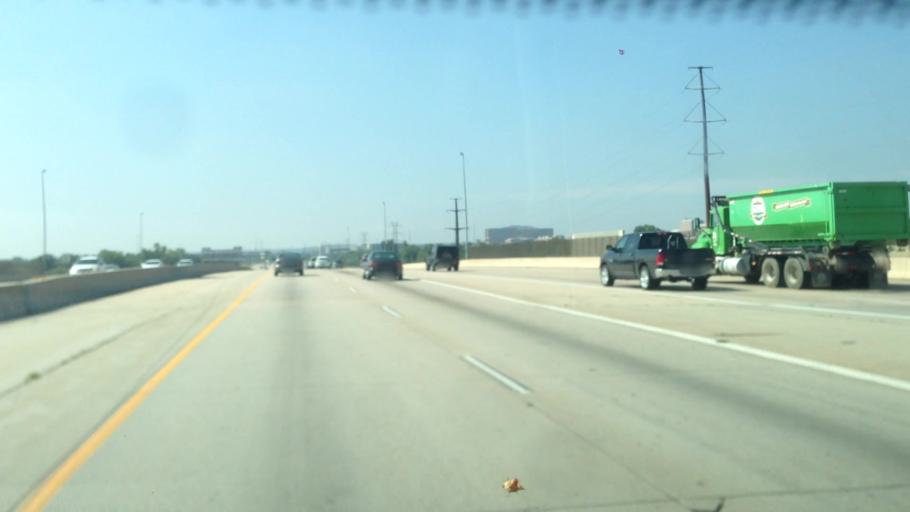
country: US
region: Colorado
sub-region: Adams County
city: Aurora
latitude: 39.7652
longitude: -104.8280
